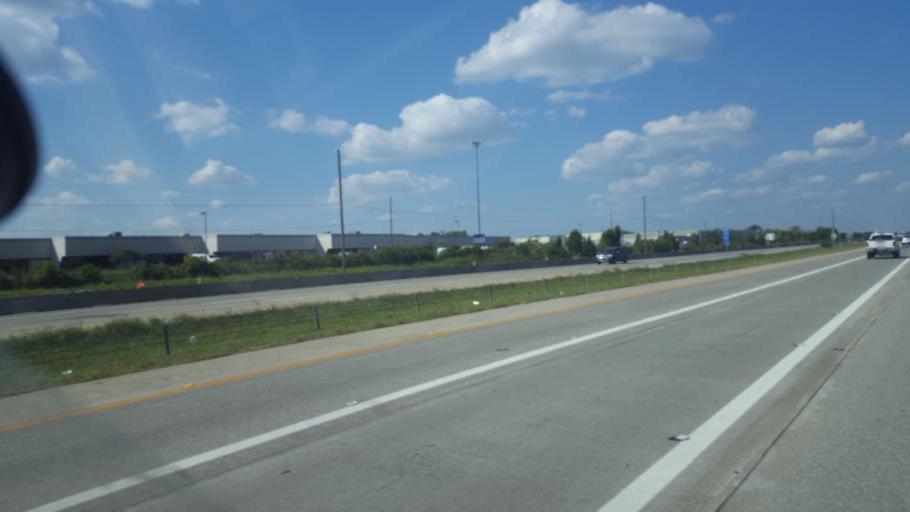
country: US
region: Ohio
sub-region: Franklin County
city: Lincoln Village
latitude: 39.9889
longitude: -83.1185
